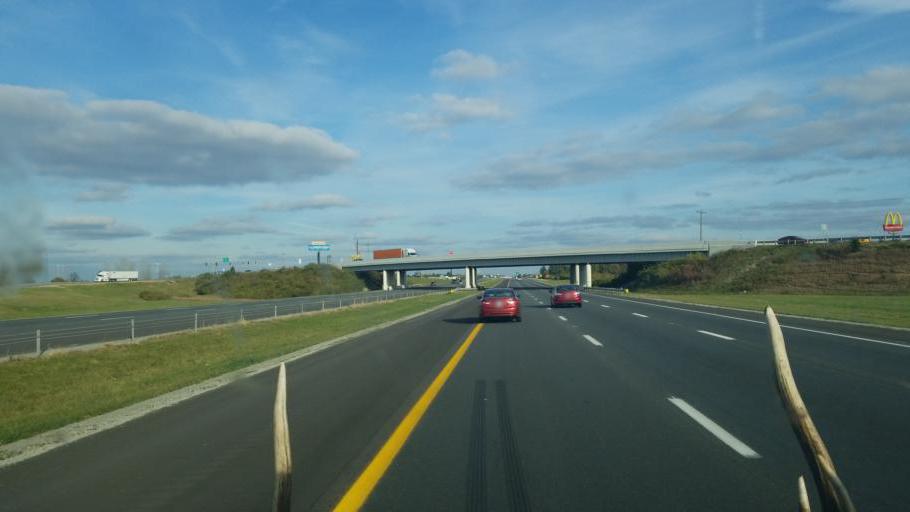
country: US
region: Ohio
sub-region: Madison County
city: London
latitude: 39.9553
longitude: -83.3772
